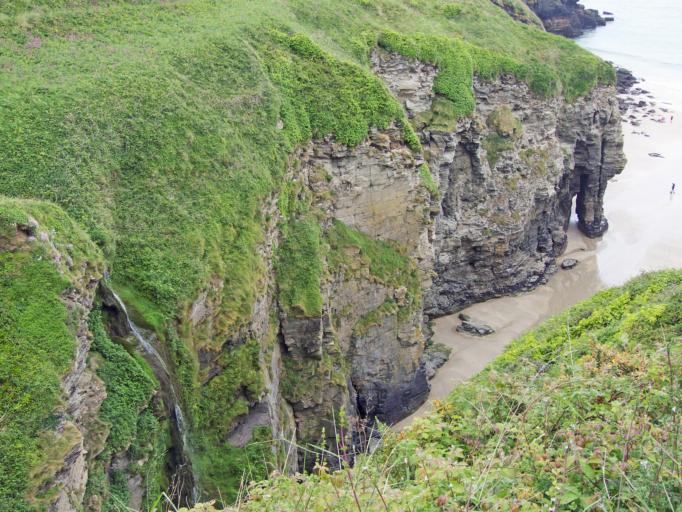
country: GB
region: England
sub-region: Cornwall
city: Tintagel
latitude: 50.6710
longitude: -4.7378
